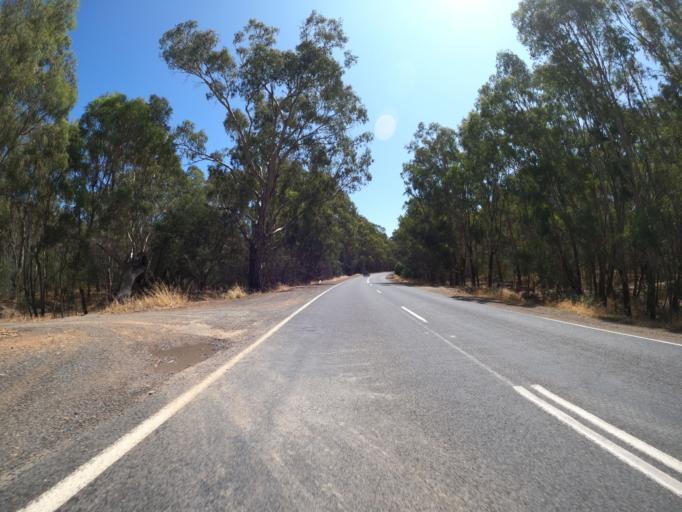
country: AU
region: New South Wales
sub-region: Corowa Shire
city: Corowa
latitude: -36.0691
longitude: 146.1982
